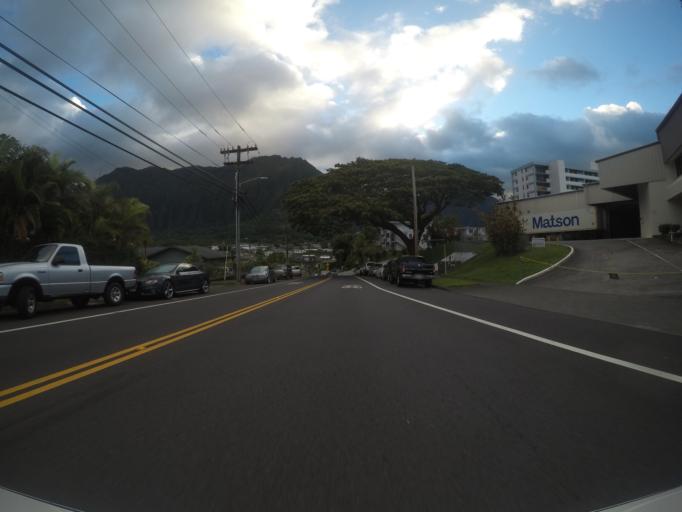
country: US
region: Hawaii
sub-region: Honolulu County
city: Kane'ohe
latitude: 21.3998
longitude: -157.8006
